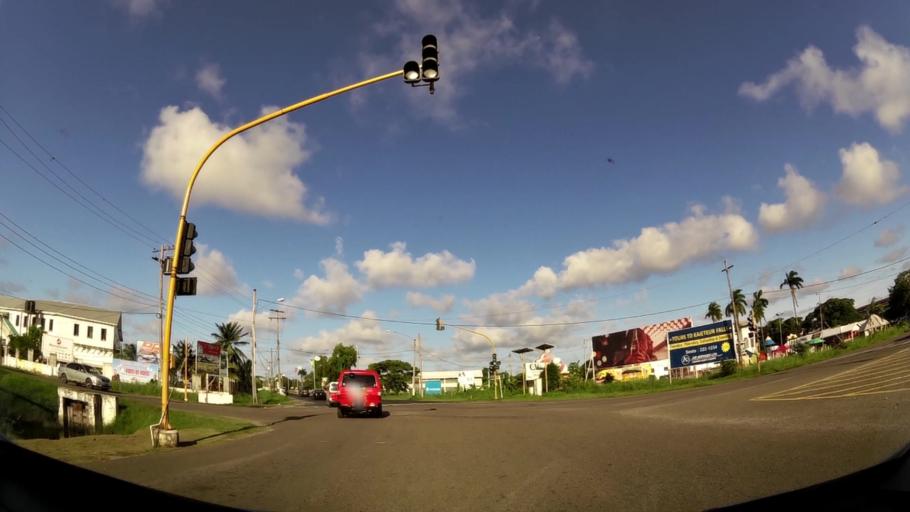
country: GY
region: Demerara-Mahaica
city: Georgetown
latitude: 6.8226
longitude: -58.1574
